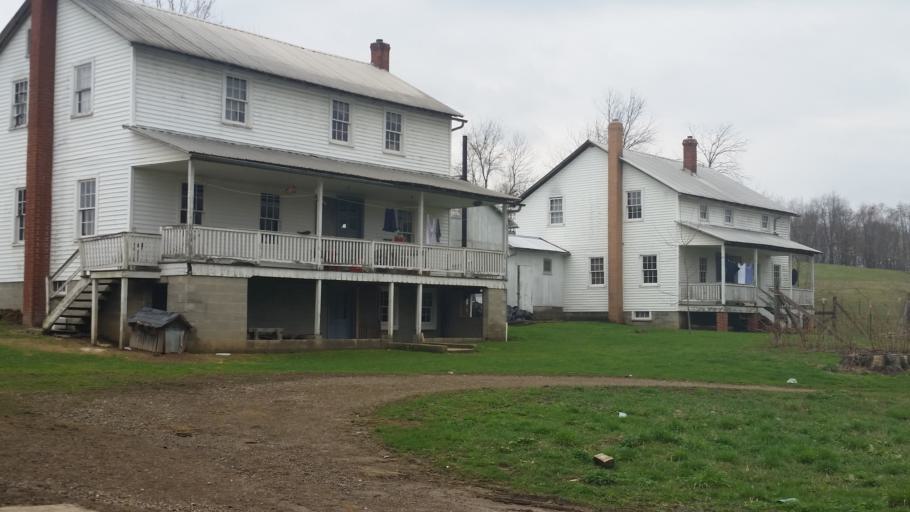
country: US
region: Ohio
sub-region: Knox County
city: Oak Hill
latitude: 40.3077
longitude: -82.2297
